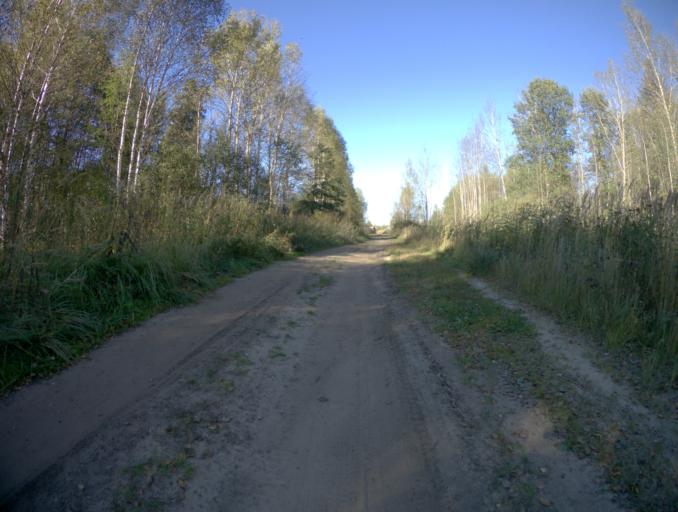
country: RU
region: Vladimir
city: Raduzhnyy
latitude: 55.9408
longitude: 40.2407
